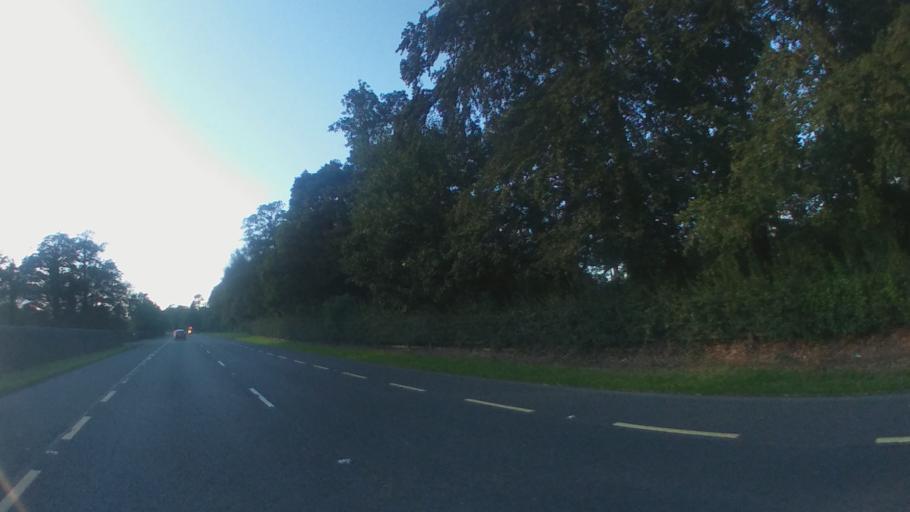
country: IE
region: Leinster
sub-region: Lu
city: Blackrock
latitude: 54.0289
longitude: -6.3518
